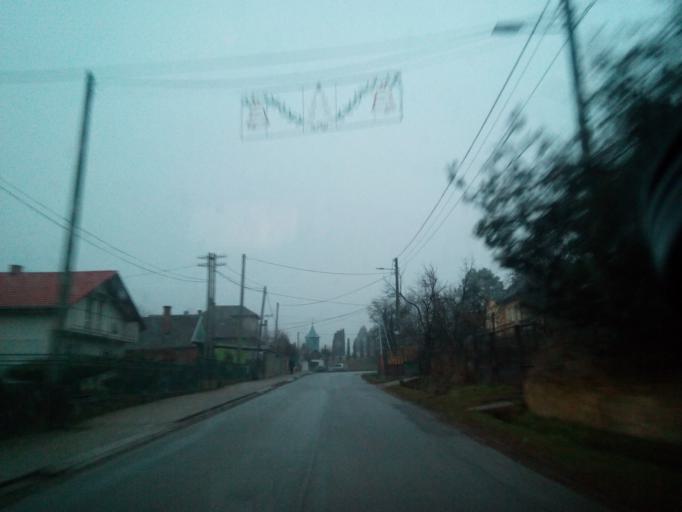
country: SK
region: Presovsky
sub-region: Okres Presov
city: Presov
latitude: 49.0354
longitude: 21.1937
